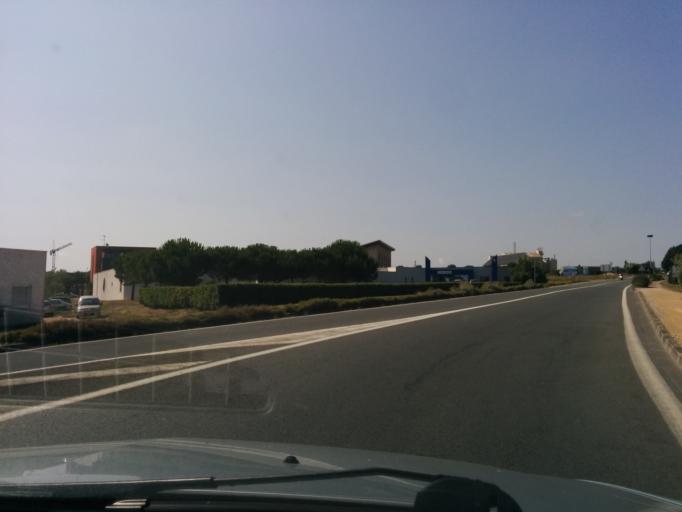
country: FR
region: Poitou-Charentes
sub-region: Departement de la Vienne
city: Jaunay-Clan
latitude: 46.6813
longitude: 0.3643
